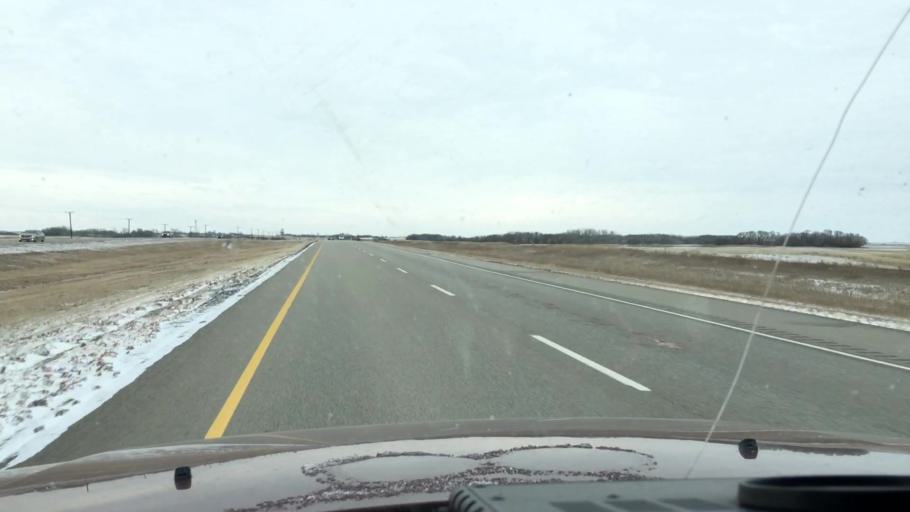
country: CA
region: Saskatchewan
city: Watrous
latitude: 51.3927
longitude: -106.1698
